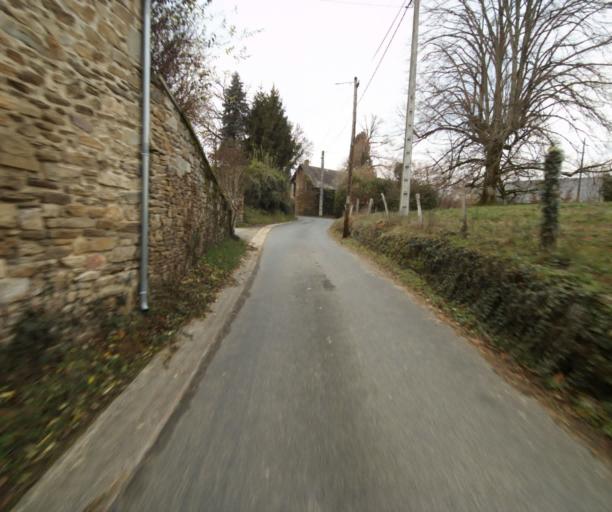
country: FR
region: Limousin
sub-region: Departement de la Correze
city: Chameyrat
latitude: 45.2423
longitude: 1.7223
